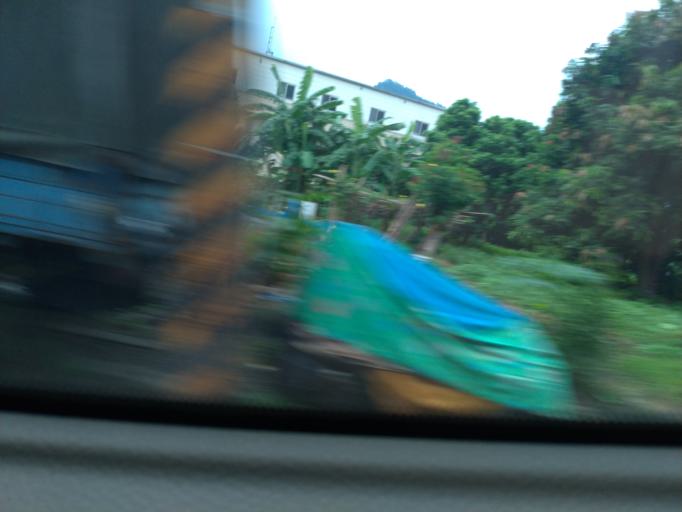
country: TW
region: Taiwan
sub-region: Taoyuan
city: Taoyuan
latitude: 24.9343
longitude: 121.4024
